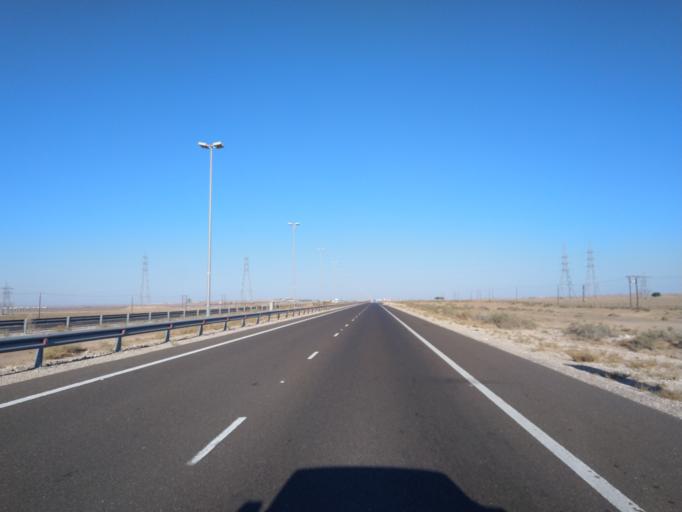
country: OM
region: Al Buraimi
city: Al Buraymi
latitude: 24.4952
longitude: 55.4236
